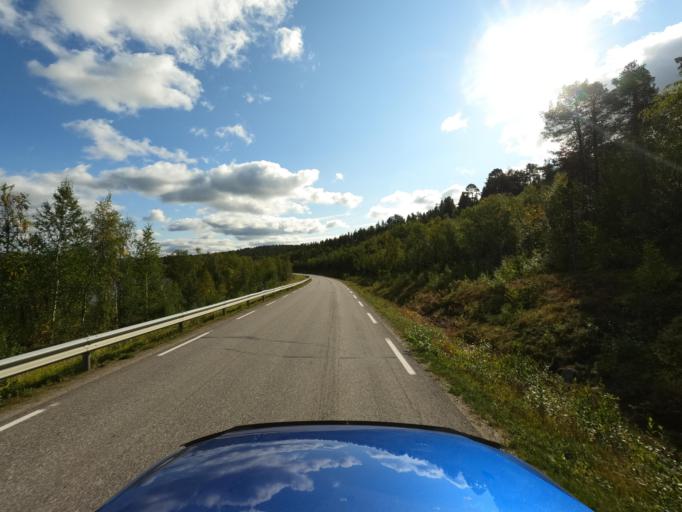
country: NO
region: Finnmark Fylke
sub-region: Karasjok
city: Karasjohka
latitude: 69.4504
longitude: 25.5845
